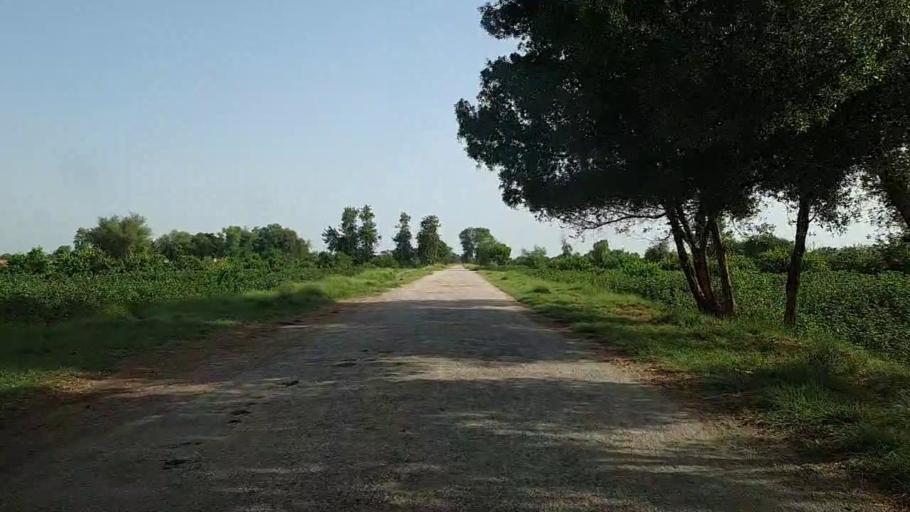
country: PK
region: Sindh
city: Karaundi
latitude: 26.8629
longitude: 68.3308
